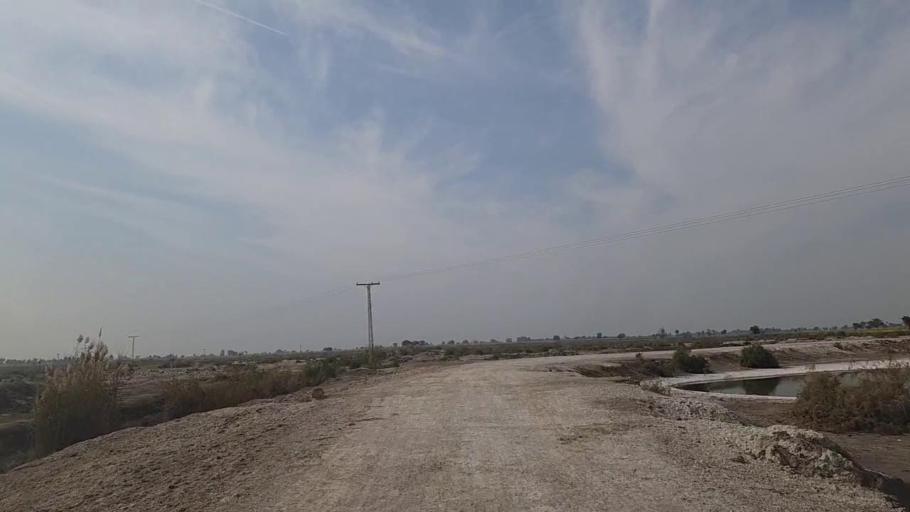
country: PK
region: Sindh
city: Daur
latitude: 26.4646
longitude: 68.4044
